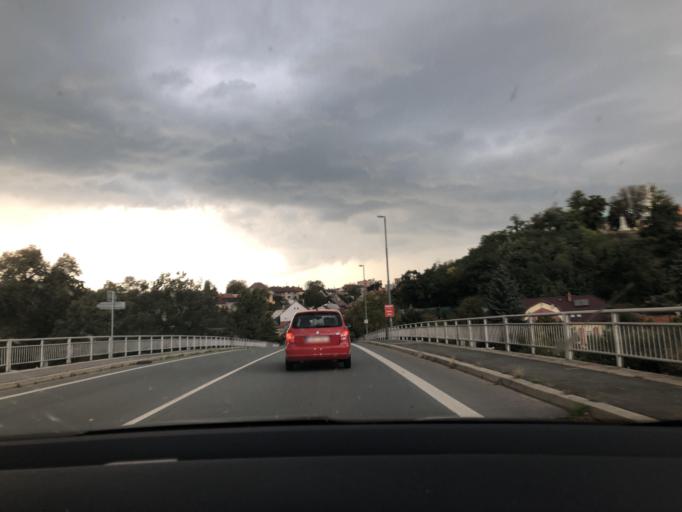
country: CZ
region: Central Bohemia
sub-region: Okres Kolin
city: Tynec nad Labem
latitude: 50.0383
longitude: 15.3596
